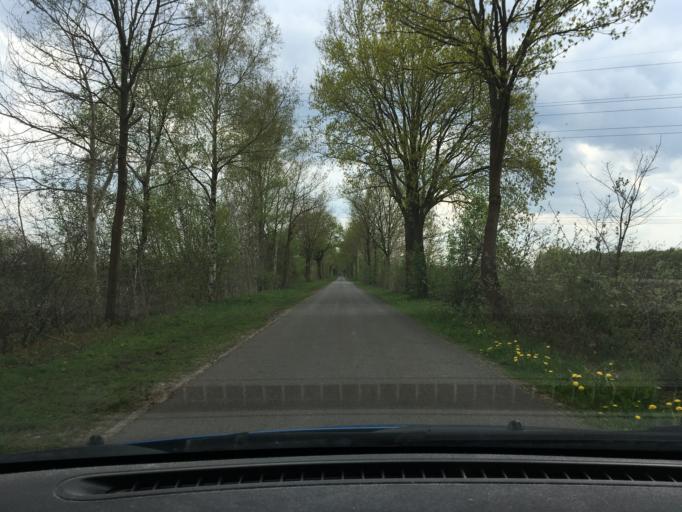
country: DE
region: Lower Saxony
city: Radbruch
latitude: 53.2989
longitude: 10.2693
